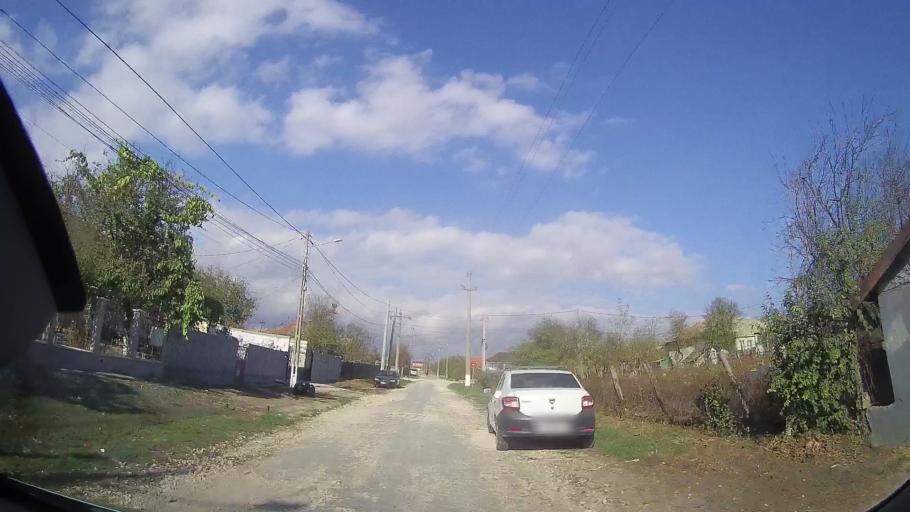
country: RO
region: Constanta
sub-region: Comuna Douazeci si Trei August
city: Douazeci si Trei August
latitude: 43.9144
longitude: 28.5865
